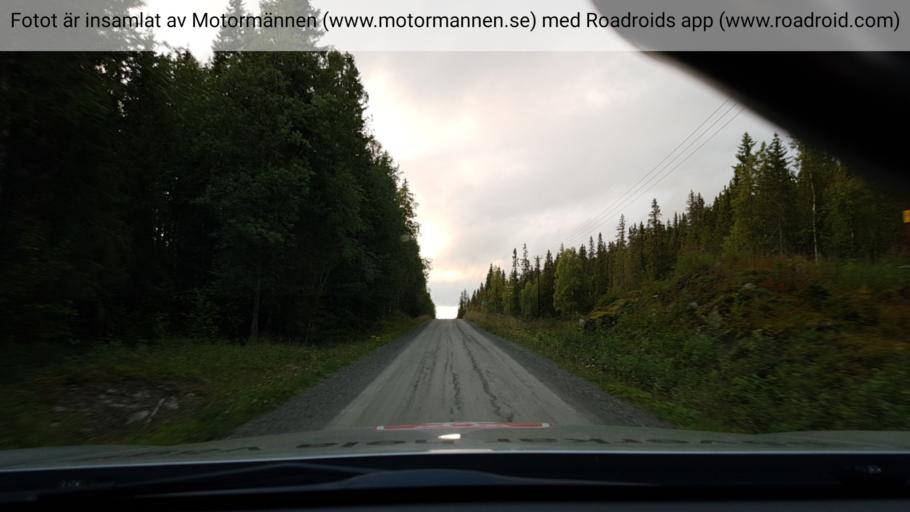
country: SE
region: Vaesterbotten
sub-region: Vilhelmina Kommun
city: Sjoberg
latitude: 65.5805
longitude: 15.3000
